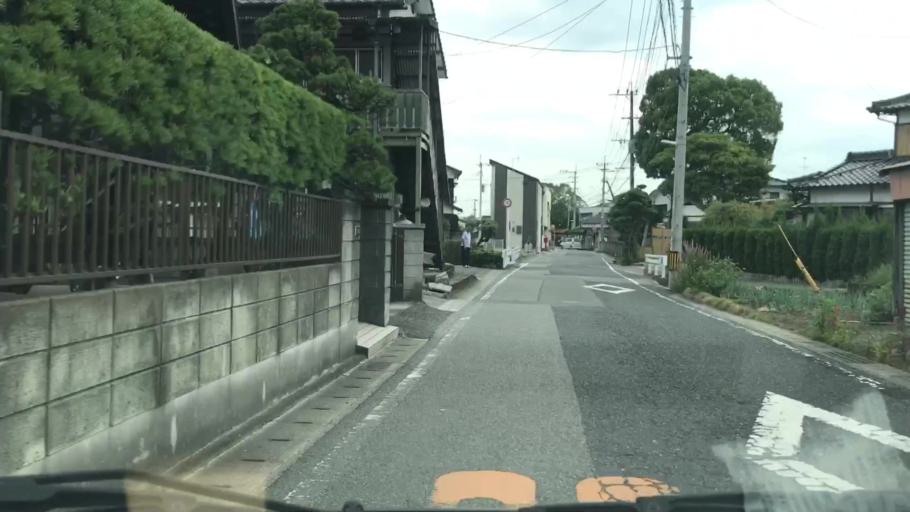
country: JP
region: Saga Prefecture
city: Saga-shi
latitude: 33.2724
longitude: 130.2634
